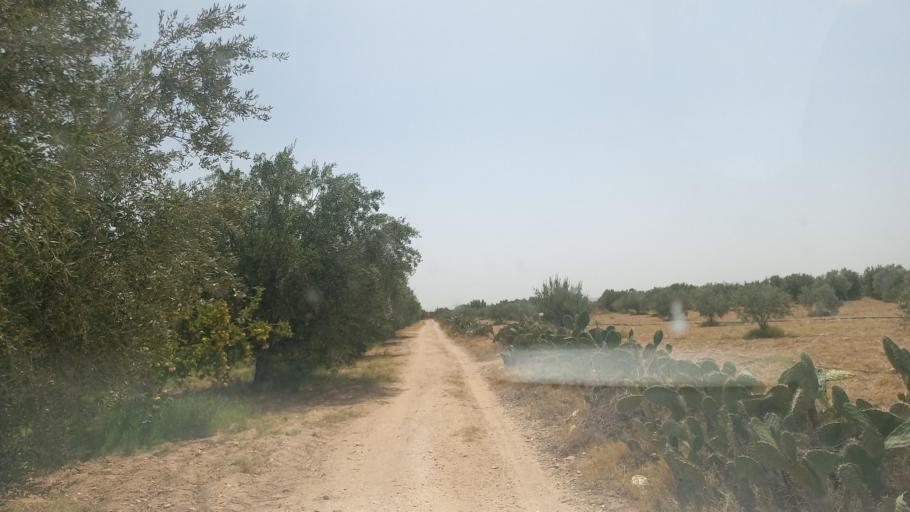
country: TN
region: Al Qasrayn
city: Kasserine
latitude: 35.2577
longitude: 9.0077
